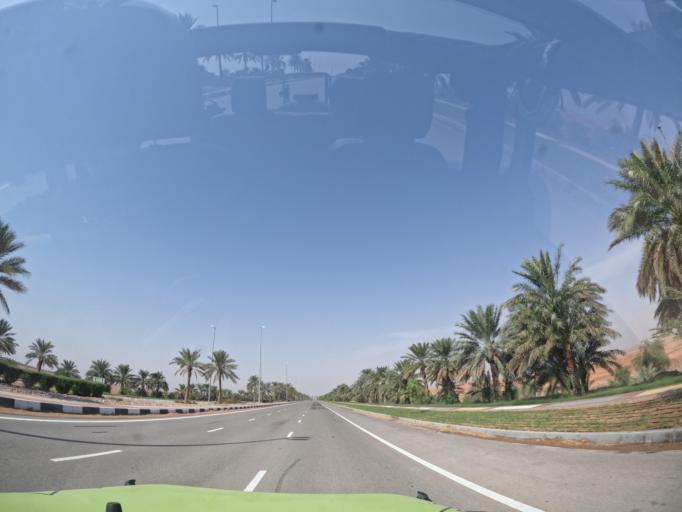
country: AE
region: Abu Dhabi
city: Al Ain
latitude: 24.2624
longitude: 55.6653
